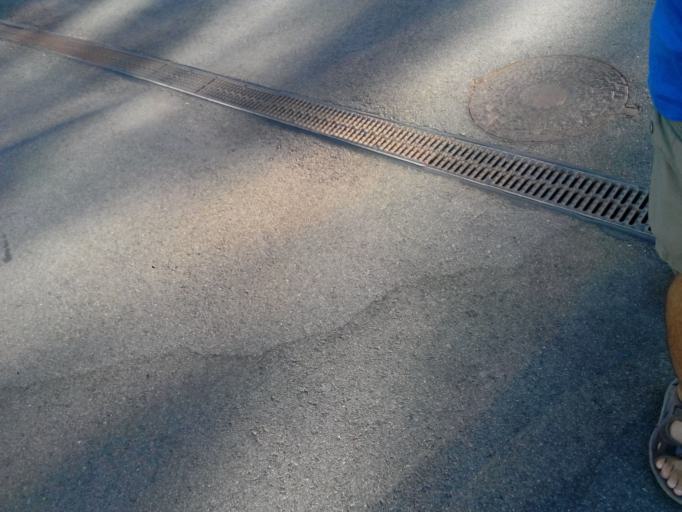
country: RO
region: Ilfov
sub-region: Comuna Fundeni-Dobroesti
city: Fundeni
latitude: 44.4364
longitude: 26.1510
